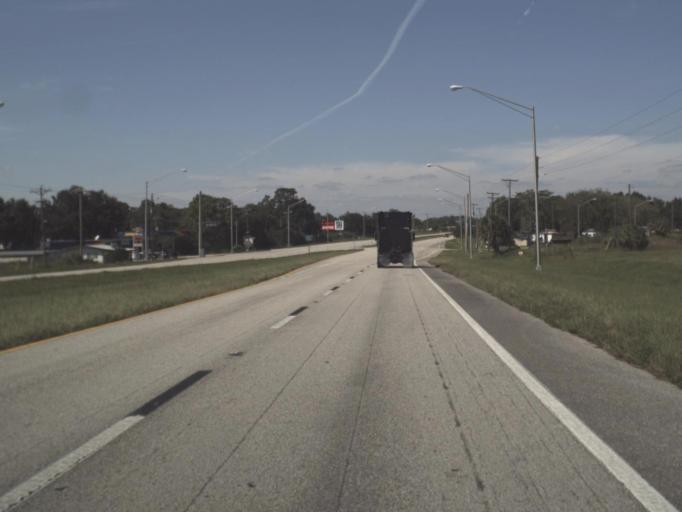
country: US
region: Florida
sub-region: Highlands County
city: Lake Placid
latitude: 27.3894
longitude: -81.4128
